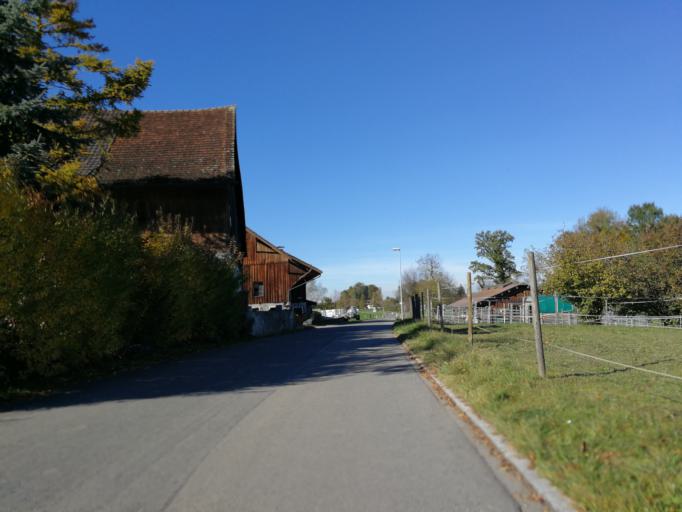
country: CH
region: Zurich
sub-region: Bezirk Uster
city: Moenchaltorf / Dorf
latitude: 47.3007
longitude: 8.7315
